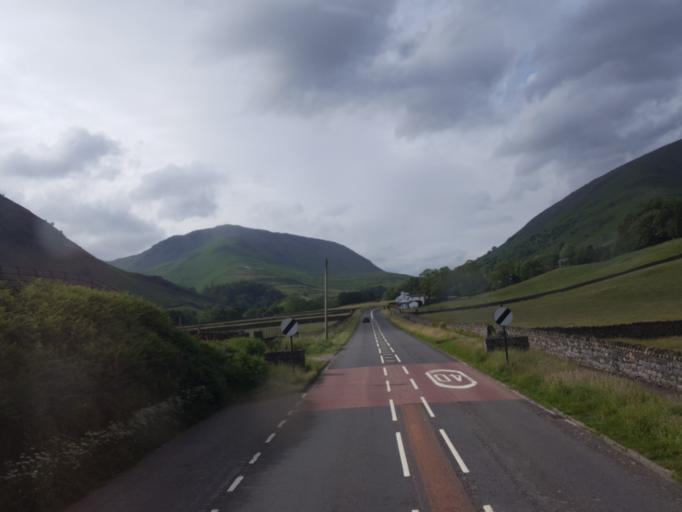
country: GB
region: England
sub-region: Cumbria
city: Ambleside
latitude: 54.4683
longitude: -3.0236
